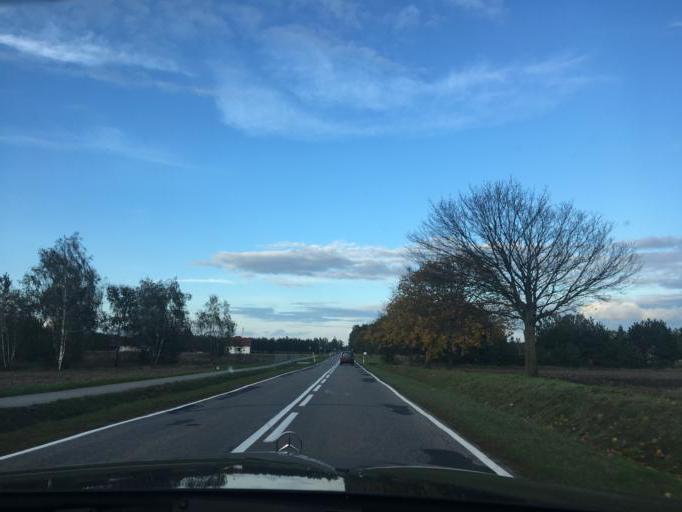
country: PL
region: Lublin Voivodeship
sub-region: Powiat bialski
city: Slawatycze
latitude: 51.7456
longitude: 23.5327
